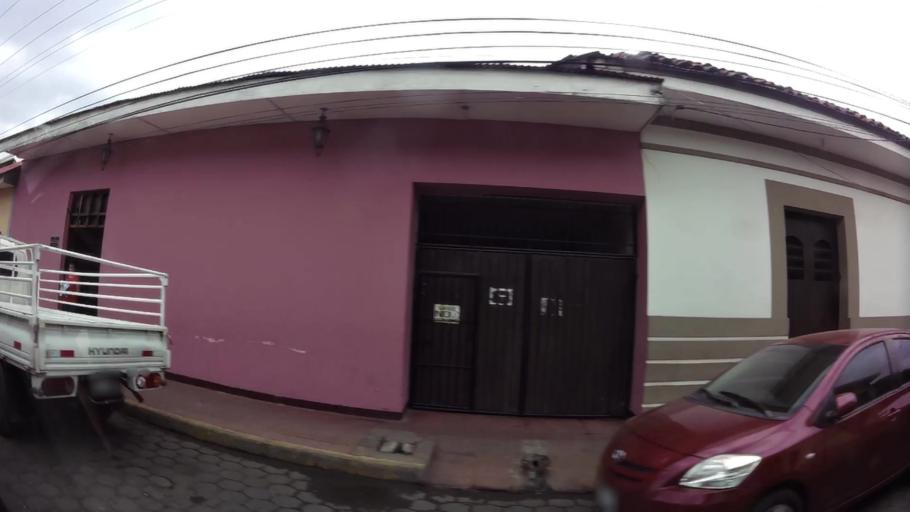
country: NI
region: Leon
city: Leon
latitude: 12.4342
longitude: -86.8764
